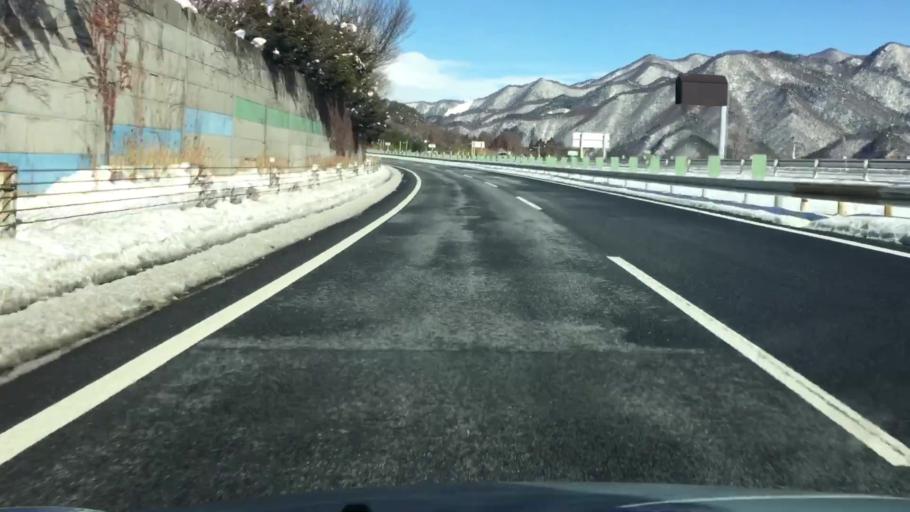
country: JP
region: Gunma
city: Numata
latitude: 36.7289
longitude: 138.9762
